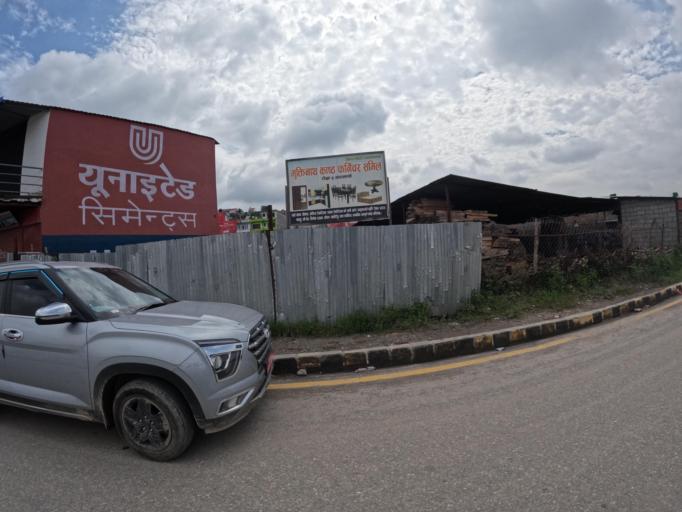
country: NP
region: Central Region
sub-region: Bagmati Zone
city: Kathmandu
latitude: 27.7599
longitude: 85.3164
